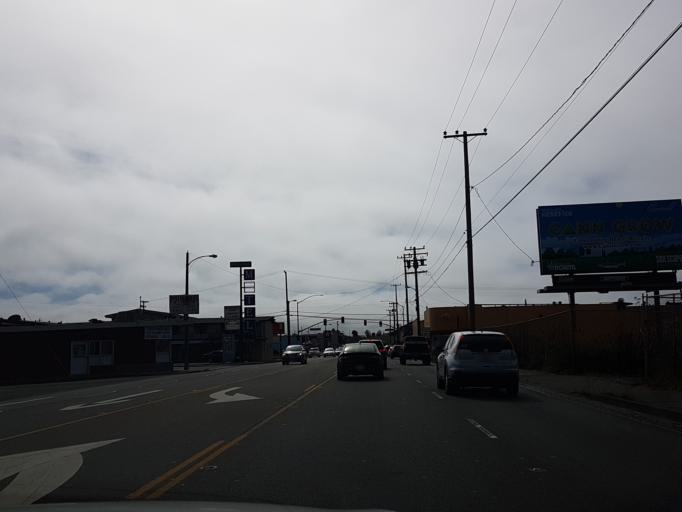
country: US
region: California
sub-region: Humboldt County
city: Eureka
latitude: 40.7996
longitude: -124.1751
